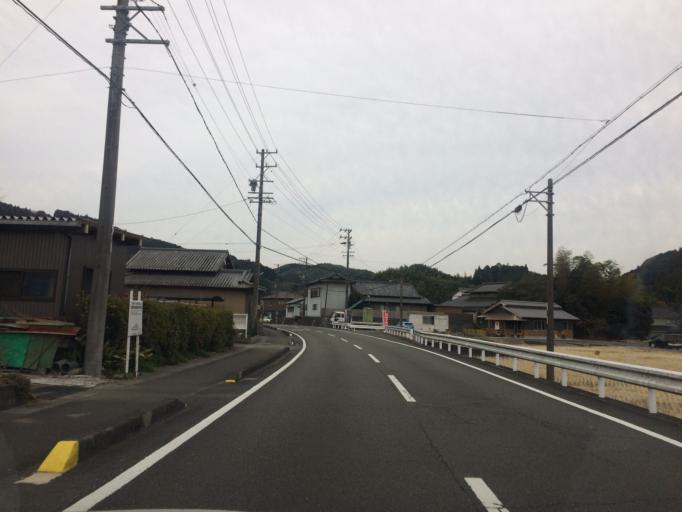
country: JP
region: Shizuoka
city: Fujieda
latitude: 34.9497
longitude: 138.2523
